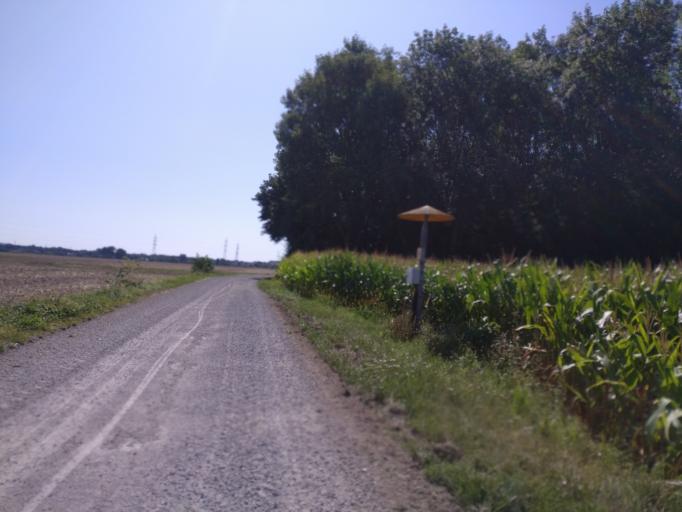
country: AT
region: Lower Austria
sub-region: Politischer Bezirk Wiener Neustadt
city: Ebenfurth
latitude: 47.8813
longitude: 16.3430
